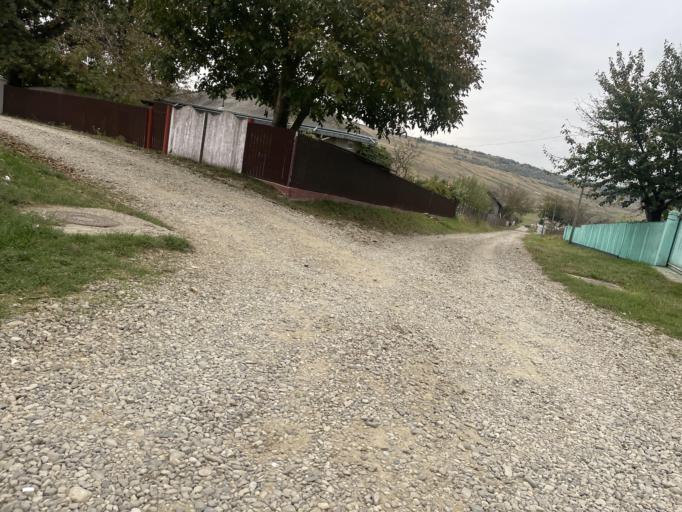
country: RO
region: Iasi
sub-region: Comuna Dumesti
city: Dumesti
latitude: 47.1747
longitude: 27.3442
